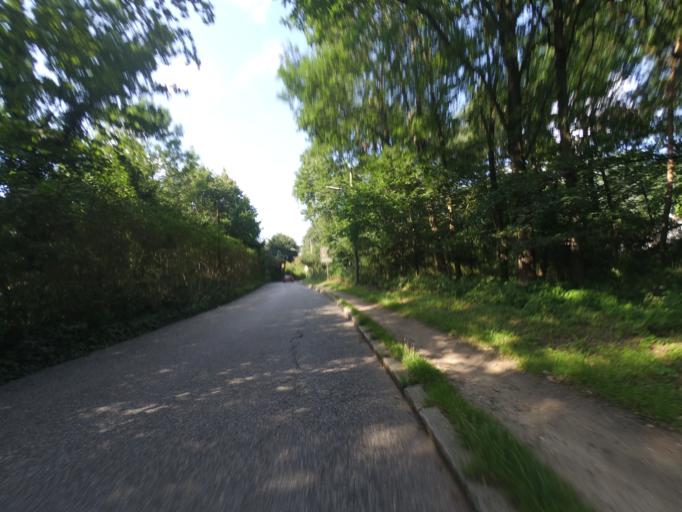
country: DE
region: Schleswig-Holstein
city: Oststeinbek
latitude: 53.5111
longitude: 10.1611
